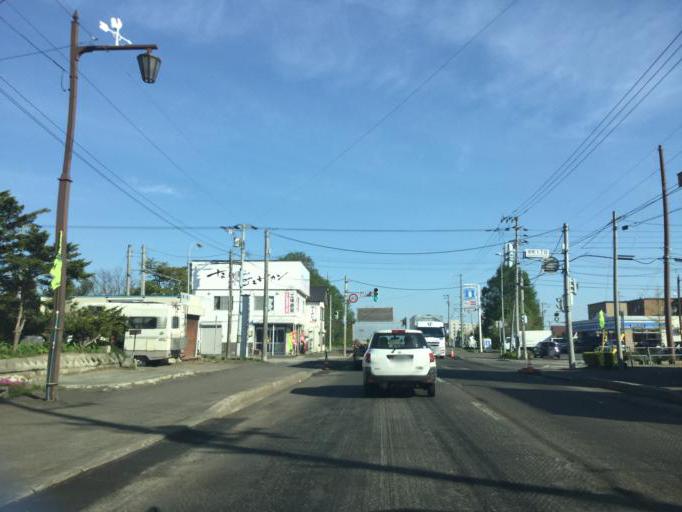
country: JP
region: Hokkaido
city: Ebetsu
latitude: 43.0646
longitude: 141.6544
